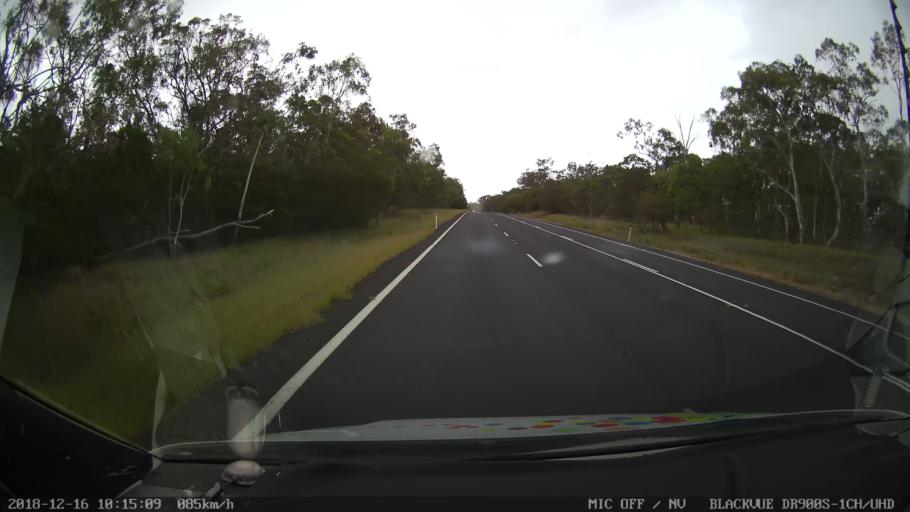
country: AU
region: New South Wales
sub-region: Tenterfield Municipality
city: Carrolls Creek
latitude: -29.2800
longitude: 151.9700
